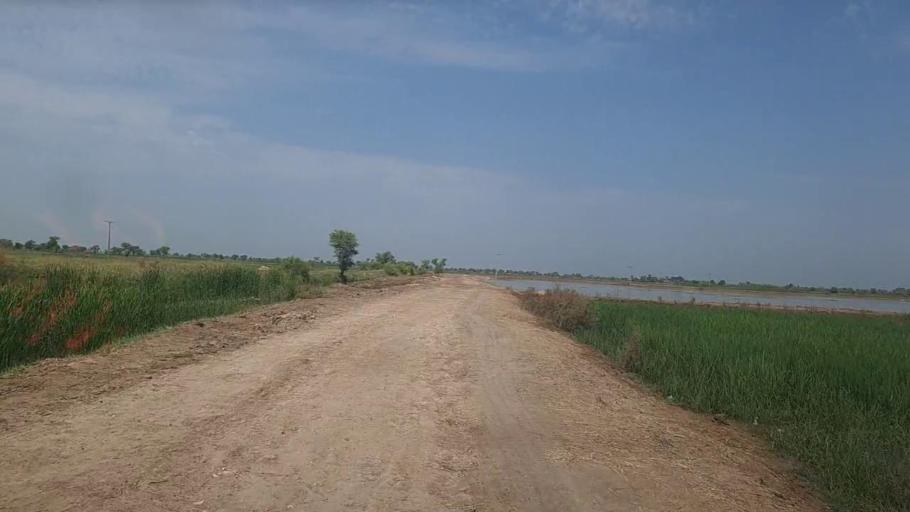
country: PK
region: Sindh
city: Thul
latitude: 28.2987
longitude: 68.6787
